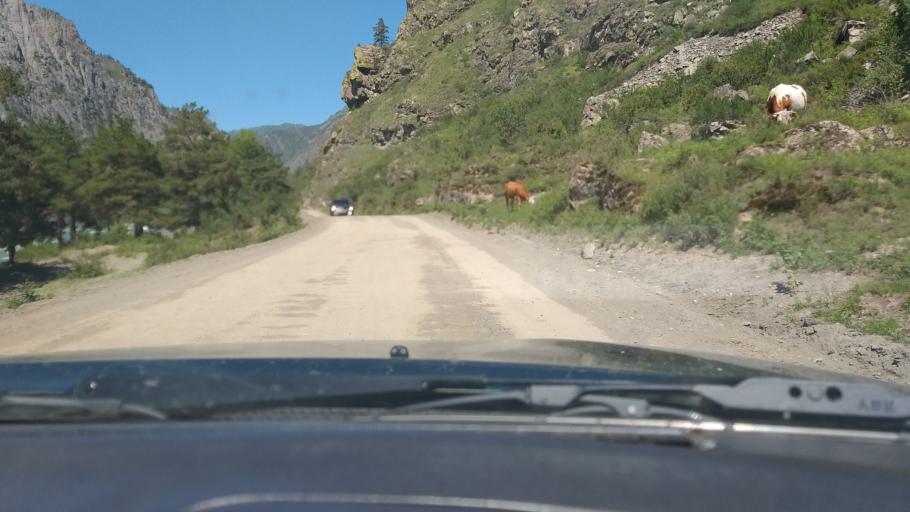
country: RU
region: Altay
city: Chemal
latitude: 51.2004
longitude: 86.0855
